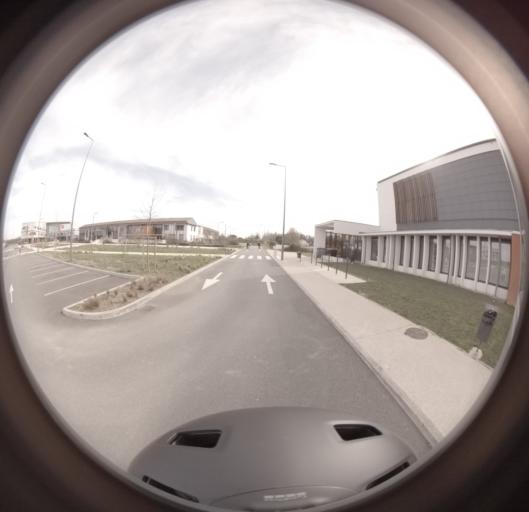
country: FR
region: Midi-Pyrenees
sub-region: Departement du Tarn-et-Garonne
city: Montech
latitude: 43.9590
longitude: 1.2497
